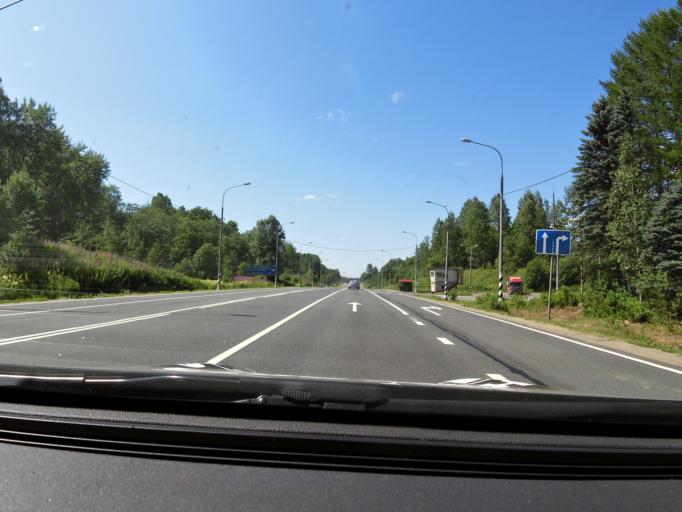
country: RU
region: Novgorod
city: Valday
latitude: 57.9978
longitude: 33.1624
